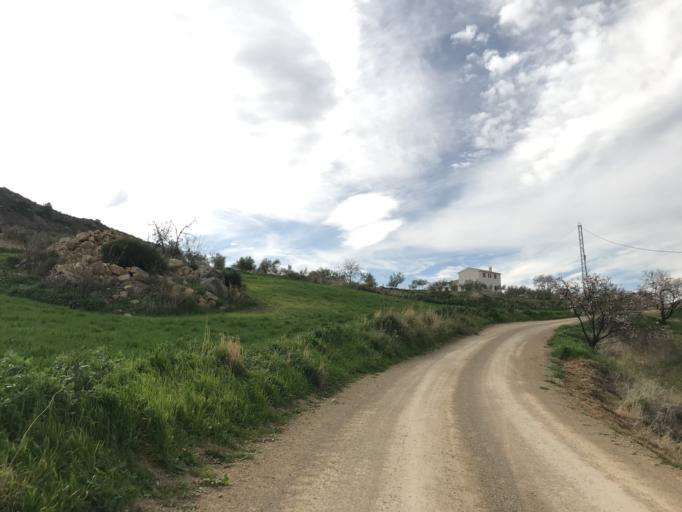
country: ES
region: Andalusia
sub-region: Provincia de Malaga
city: Ardales
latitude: 36.8776
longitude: -4.8747
